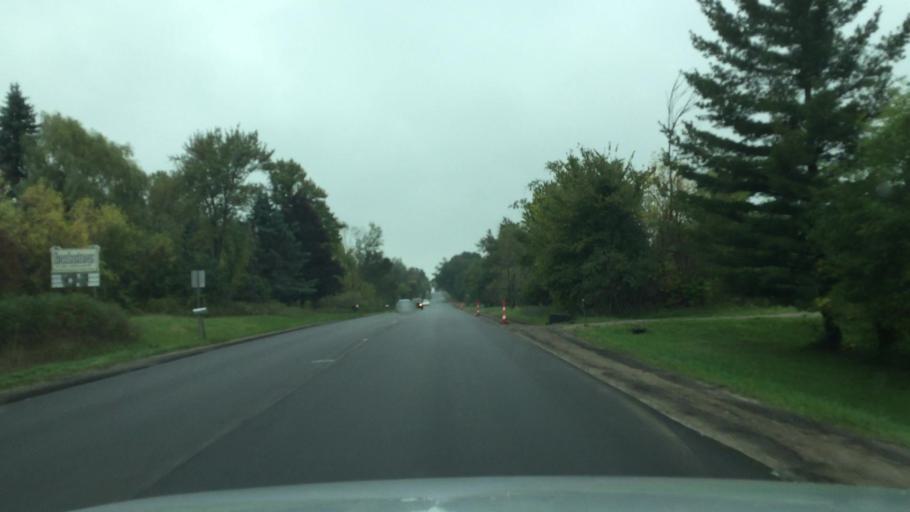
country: US
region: Michigan
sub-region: Shiawassee County
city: Perry
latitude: 42.9015
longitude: -84.2221
